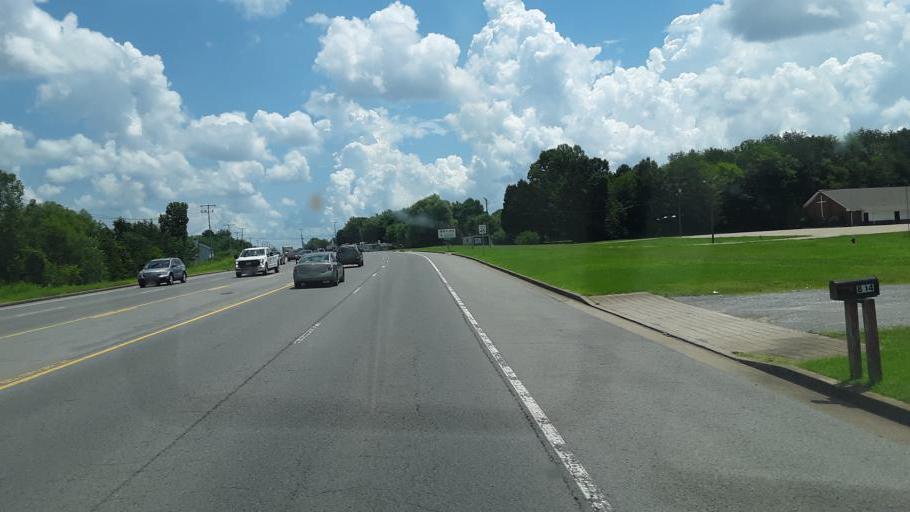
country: US
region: Kentucky
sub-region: Christian County
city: Oak Grove
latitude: 36.6317
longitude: -87.4067
